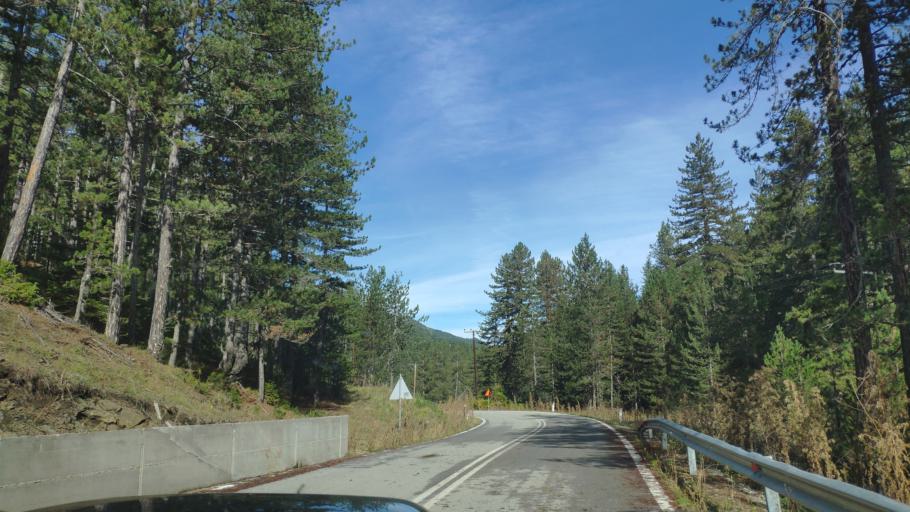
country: AL
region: Korce
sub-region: Rrethi i Devollit
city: Miras
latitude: 40.4031
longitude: 20.8805
